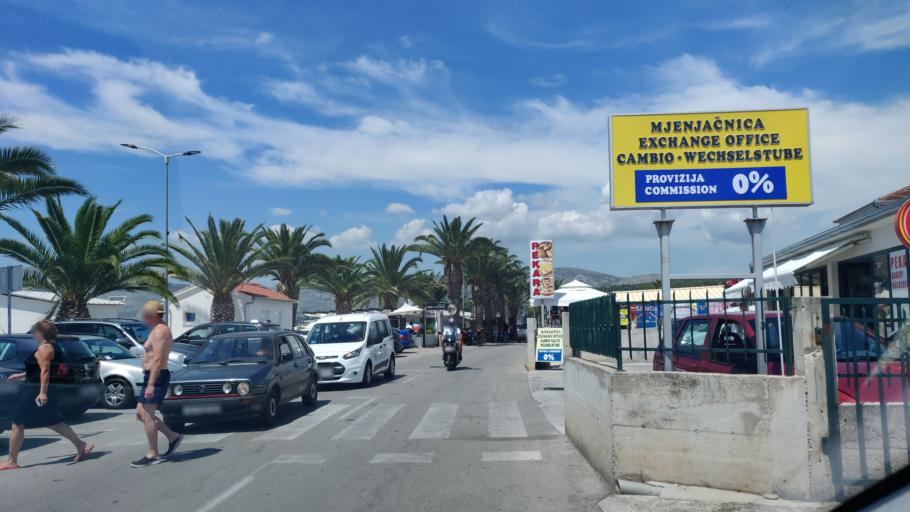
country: HR
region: Splitsko-Dalmatinska
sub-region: Grad Trogir
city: Trogir
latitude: 43.4966
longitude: 16.2607
